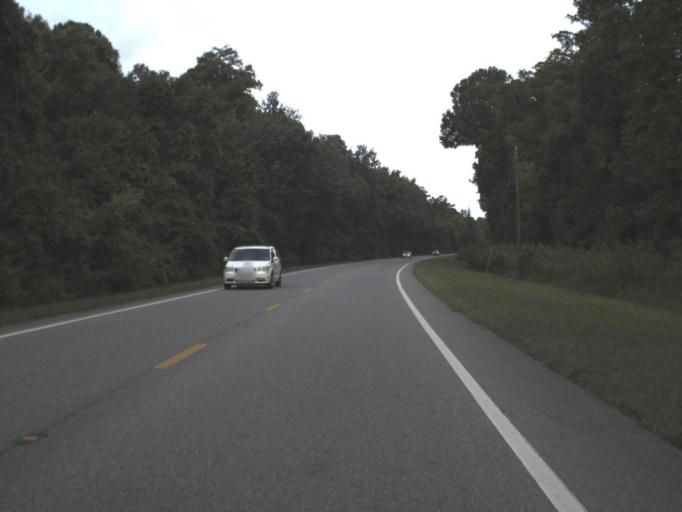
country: US
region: Florida
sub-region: Hernando County
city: Ridge Manor
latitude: 28.5083
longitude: -82.1149
